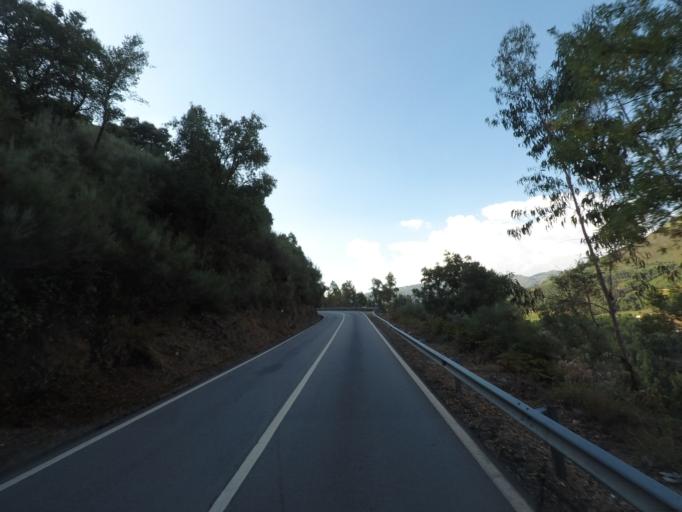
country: PT
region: Vila Real
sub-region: Mesao Frio
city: Mesao Frio
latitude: 41.1744
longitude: -7.9152
